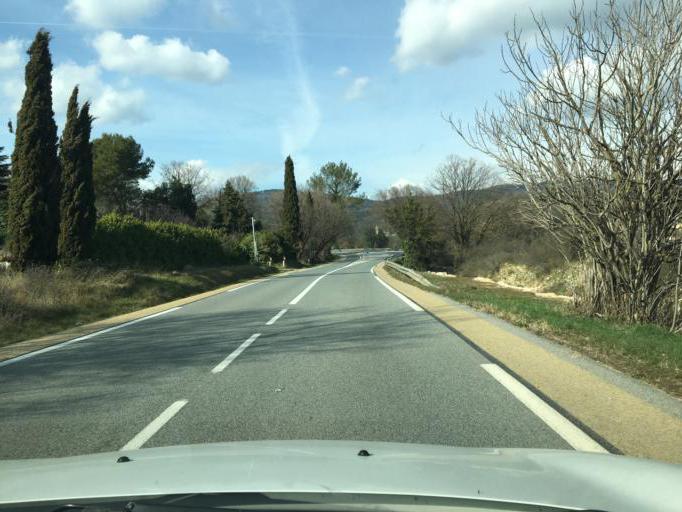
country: FR
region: Provence-Alpes-Cote d'Azur
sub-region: Departement du Var
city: Figanieres
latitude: 43.5599
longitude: 6.5129
